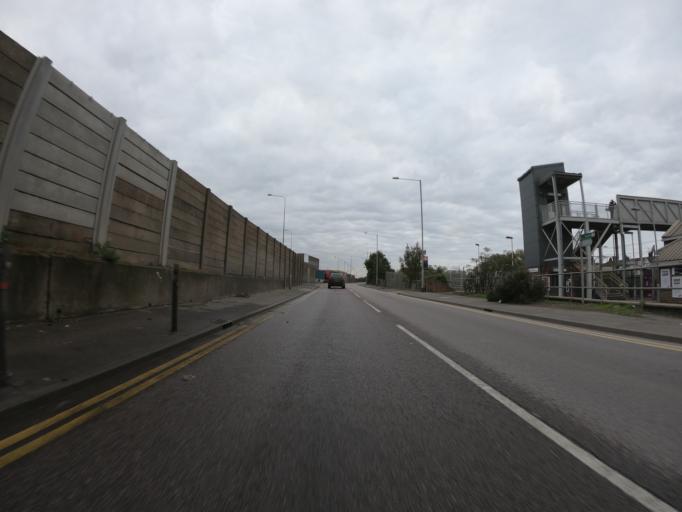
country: GB
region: England
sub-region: Borough of Thurrock
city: Tilbury
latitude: 51.4621
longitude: 0.3539
